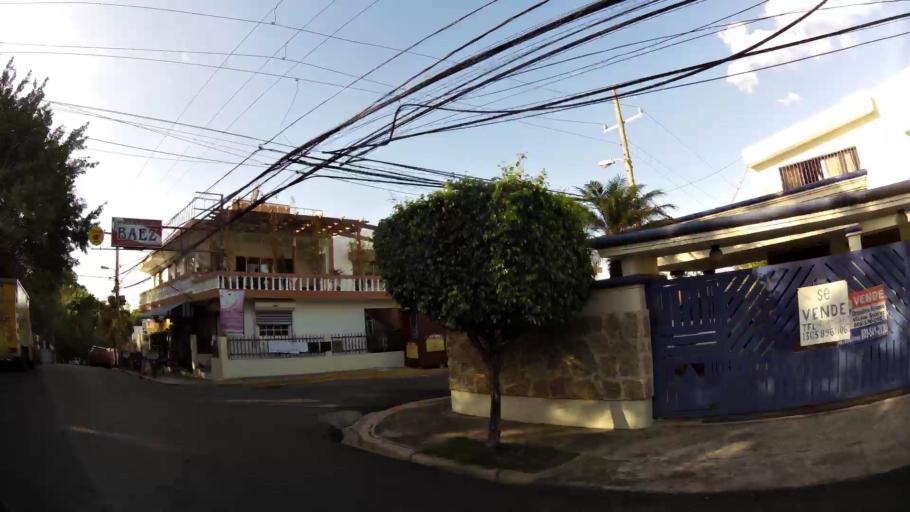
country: DO
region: Nacional
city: Santo Domingo
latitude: 18.4956
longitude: -69.9721
